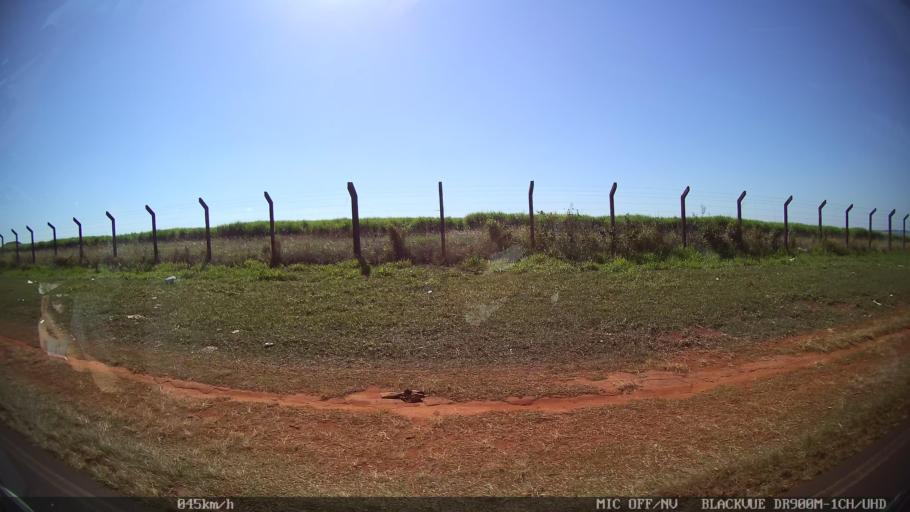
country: BR
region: Sao Paulo
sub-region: Batatais
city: Batatais
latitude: -20.8775
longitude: -47.5777
